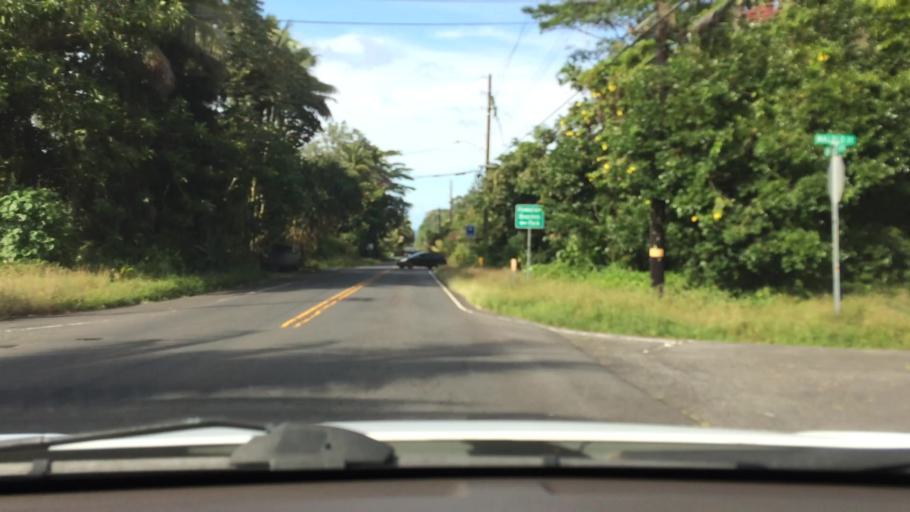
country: US
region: Hawaii
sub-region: Hawaii County
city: Hawaiian Beaches
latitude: 19.5456
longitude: -154.9034
